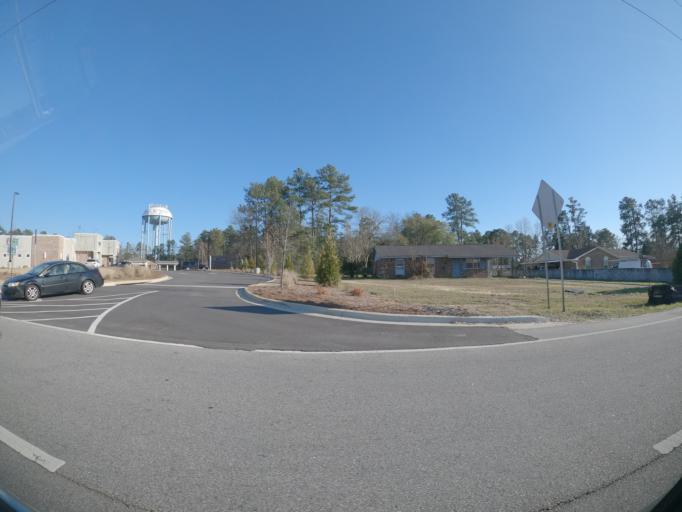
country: US
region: Georgia
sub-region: Columbia County
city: Grovetown
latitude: 33.4539
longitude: -82.2081
